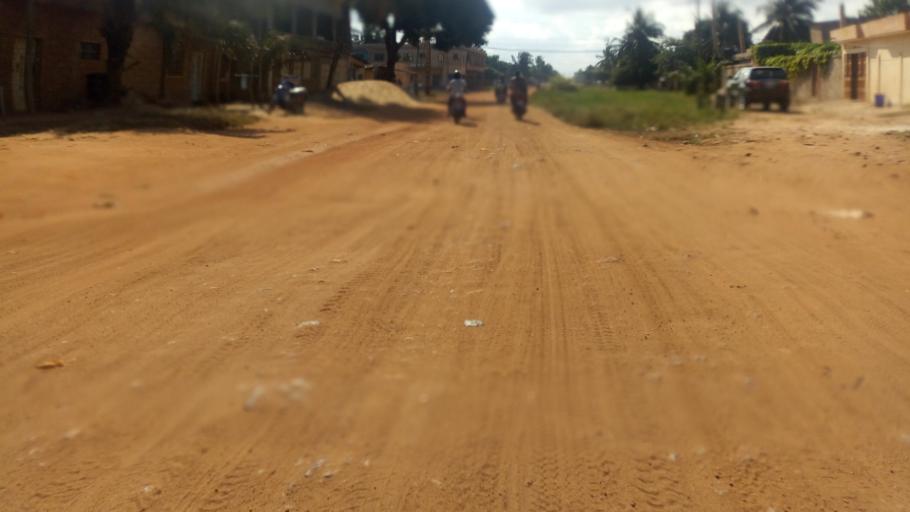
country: TG
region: Maritime
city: Lome
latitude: 6.2255
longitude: 1.1873
